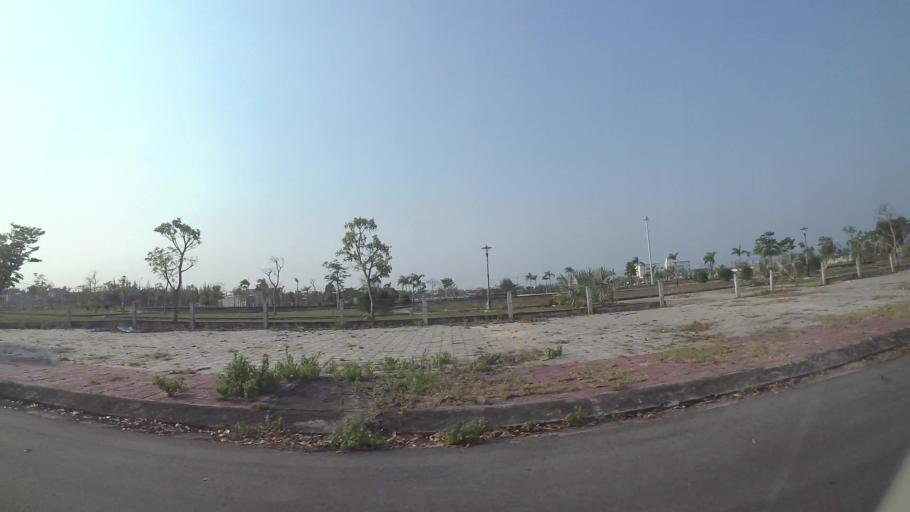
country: VN
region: Da Nang
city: Ngu Hanh Son
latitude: 15.9588
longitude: 108.2585
